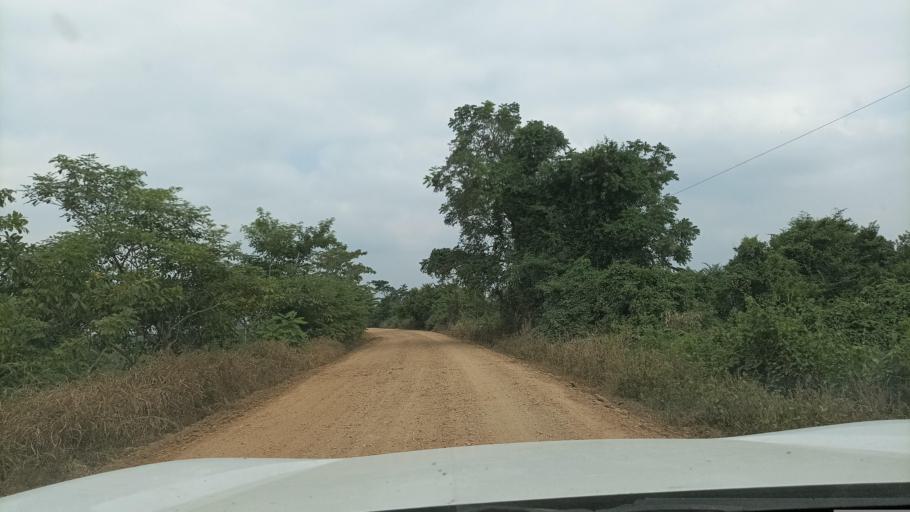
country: MX
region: Veracruz
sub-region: Texistepec
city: San Lorenzo Tenochtitlan
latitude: 17.7746
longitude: -94.7996
